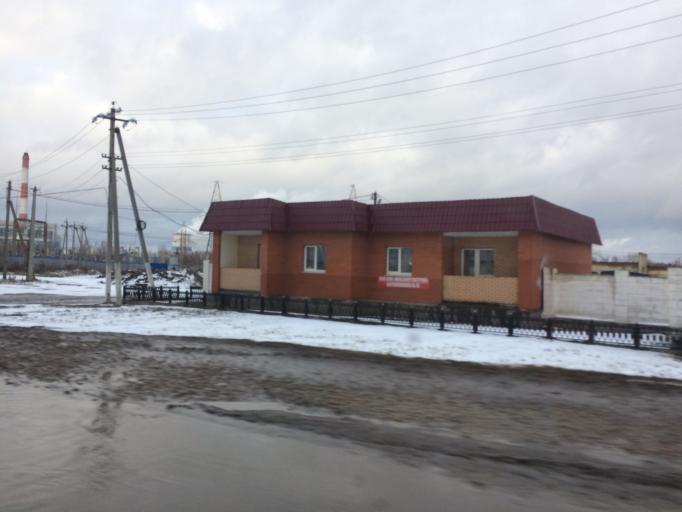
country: RU
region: Tula
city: Suvorov
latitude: 54.1264
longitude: 36.4841
